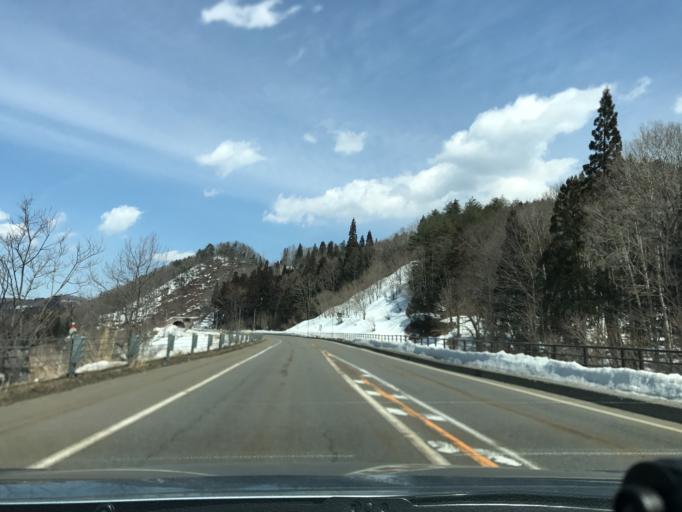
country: JP
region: Nagano
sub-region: Kitaazumi Gun
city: Hakuba
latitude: 36.6059
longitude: 137.8557
